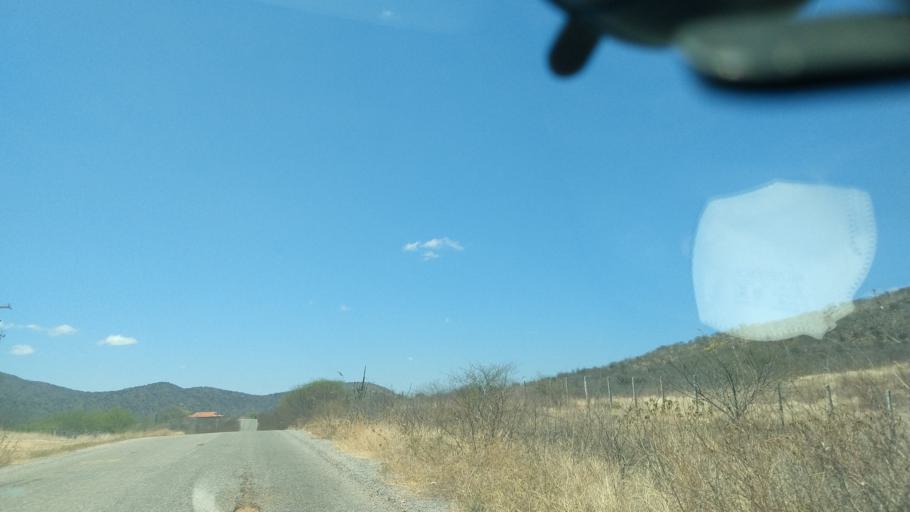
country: BR
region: Rio Grande do Norte
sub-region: Sao Tome
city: Sao Tome
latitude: -5.9751
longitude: -36.1416
